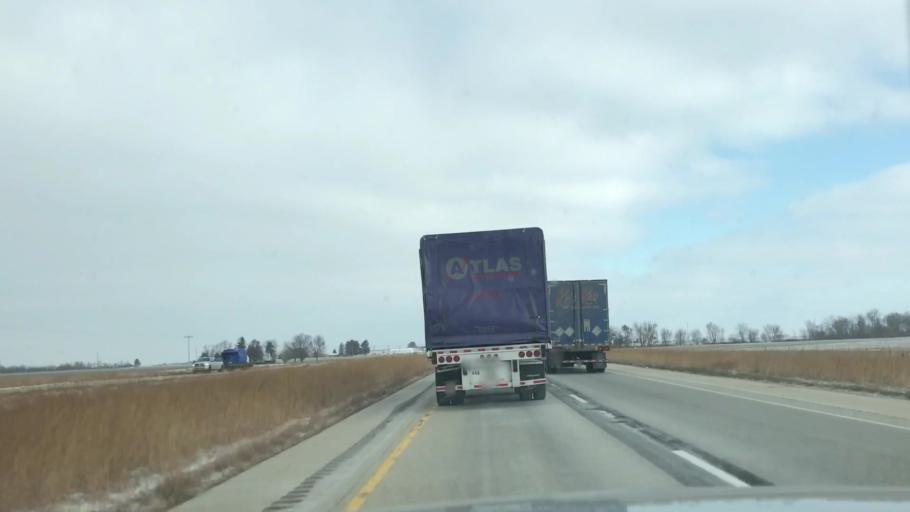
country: US
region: Illinois
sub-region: Sangamon County
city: Divernon
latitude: 39.5146
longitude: -89.6453
